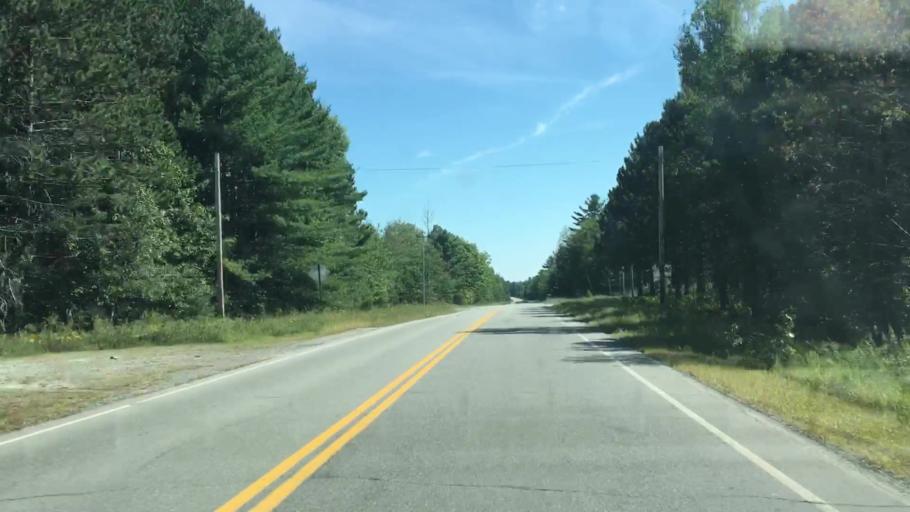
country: US
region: Maine
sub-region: Piscataquis County
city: Milo
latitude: 45.2274
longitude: -68.9317
